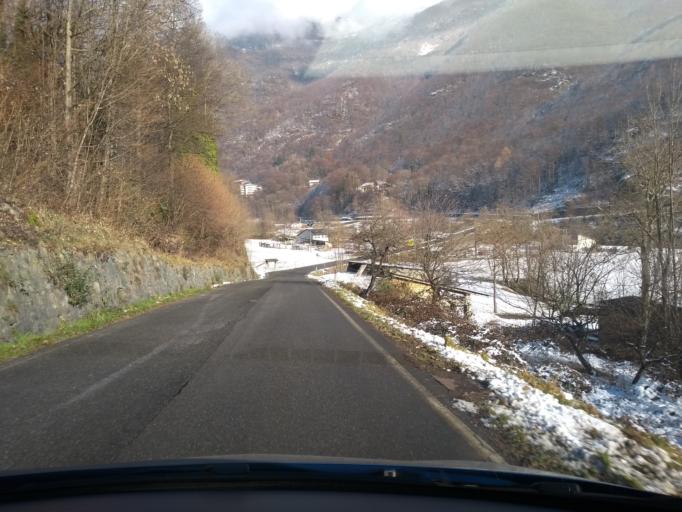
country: IT
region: Piedmont
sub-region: Provincia di Torino
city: Ceres
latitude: 45.3187
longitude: 7.3920
